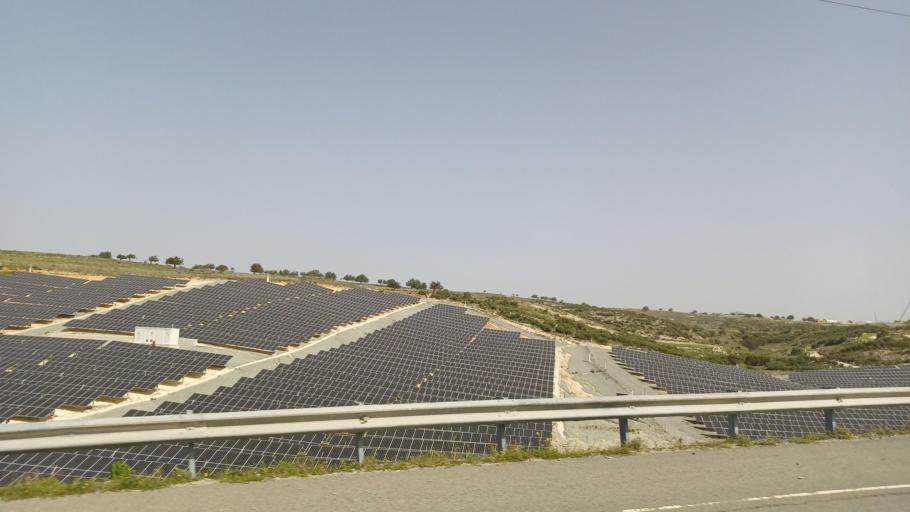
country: CY
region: Limassol
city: Pissouri
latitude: 34.6847
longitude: 32.7001
